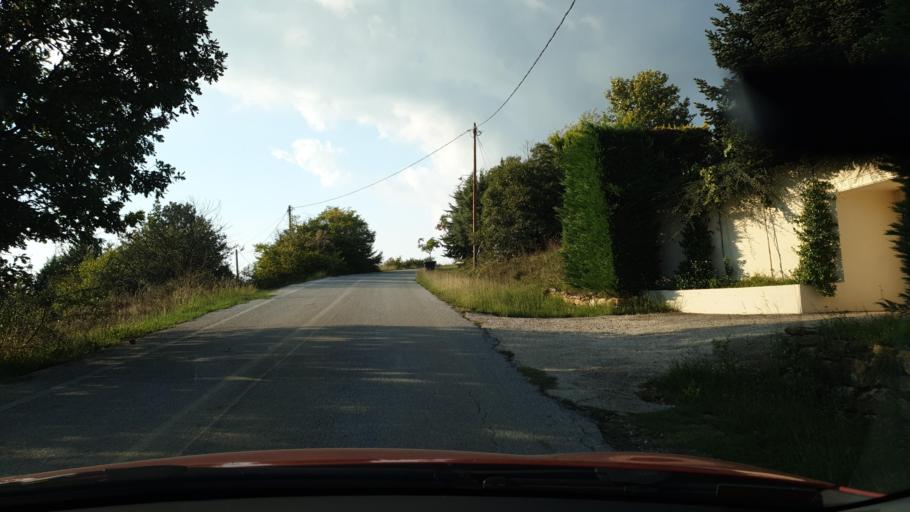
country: GR
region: Central Macedonia
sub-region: Nomos Chalkidikis
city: Galatista
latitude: 40.5253
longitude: 23.2777
